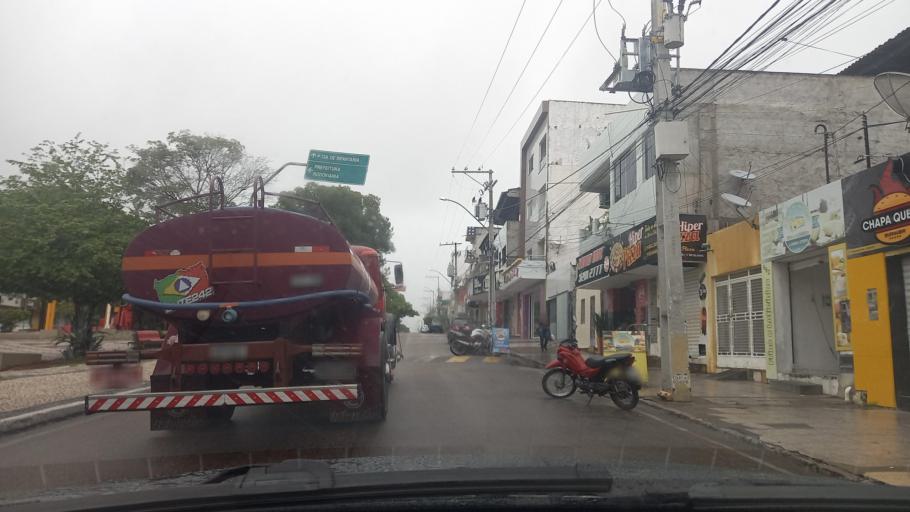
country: BR
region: Bahia
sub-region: Paulo Afonso
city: Paulo Afonso
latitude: -9.4047
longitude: -38.2161
